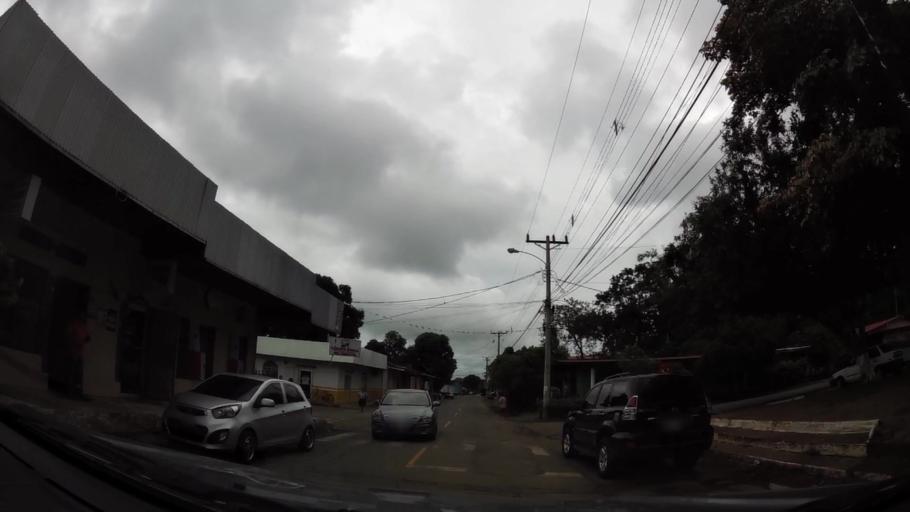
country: PA
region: Chiriqui
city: Dolega District
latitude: 8.5631
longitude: -82.4144
